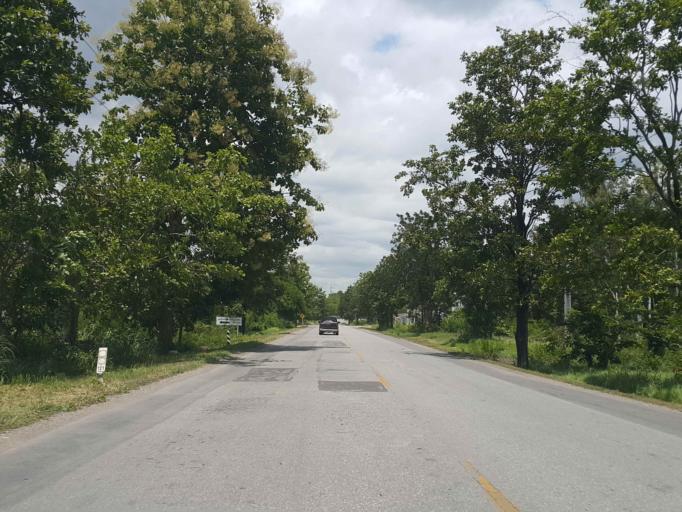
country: TH
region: Lamphun
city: Ban Hong
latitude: 18.3778
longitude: 98.8155
